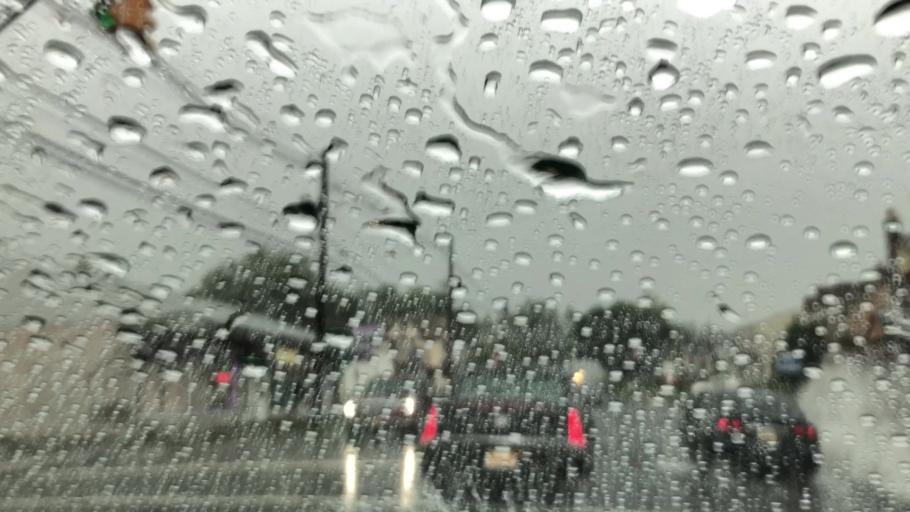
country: US
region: New Jersey
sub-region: Bergen County
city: Saddle Brook
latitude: 40.8961
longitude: -74.0882
